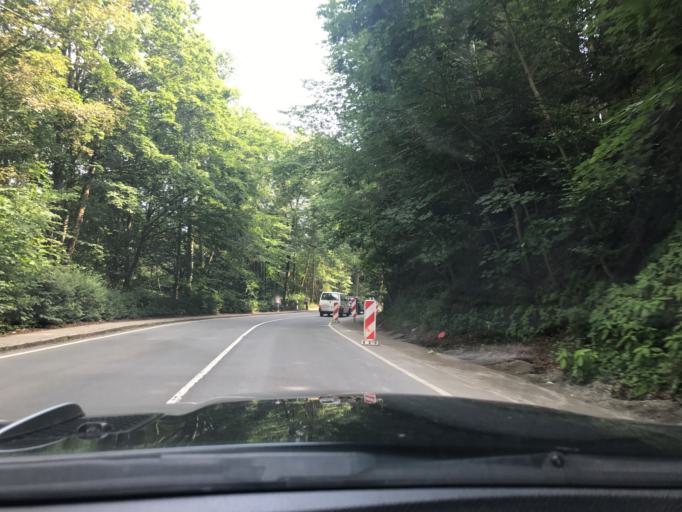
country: DE
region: Saxony-Anhalt
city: Huttenrode
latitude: 51.7390
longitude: 10.8976
